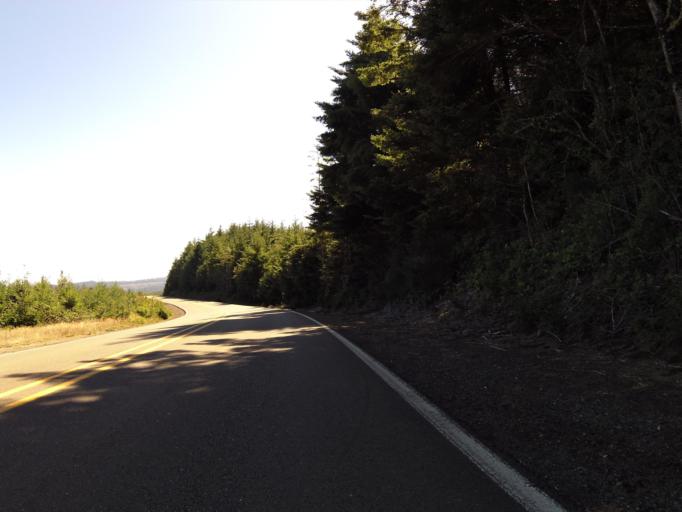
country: US
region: Oregon
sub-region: Coos County
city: Barview
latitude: 43.2505
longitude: -124.3369
